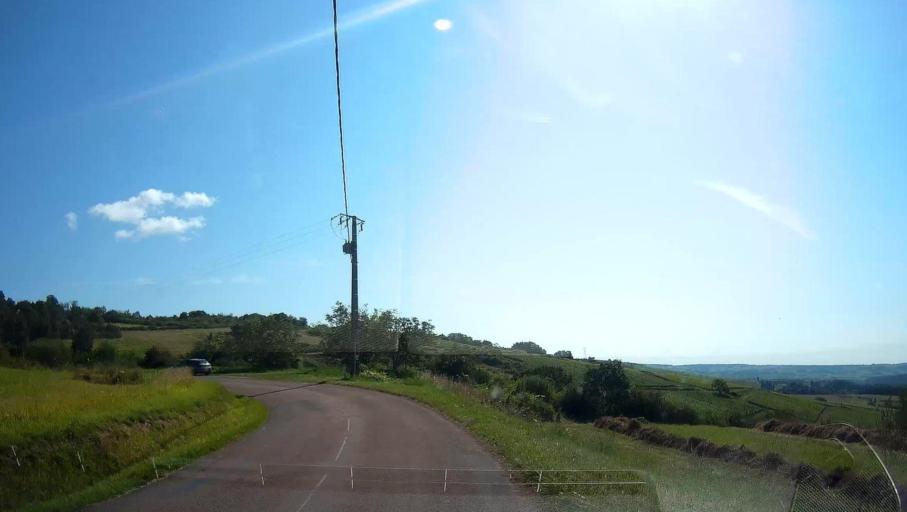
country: FR
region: Bourgogne
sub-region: Departement de Saone-et-Loire
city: Couches
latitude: 46.8899
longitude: 4.5814
